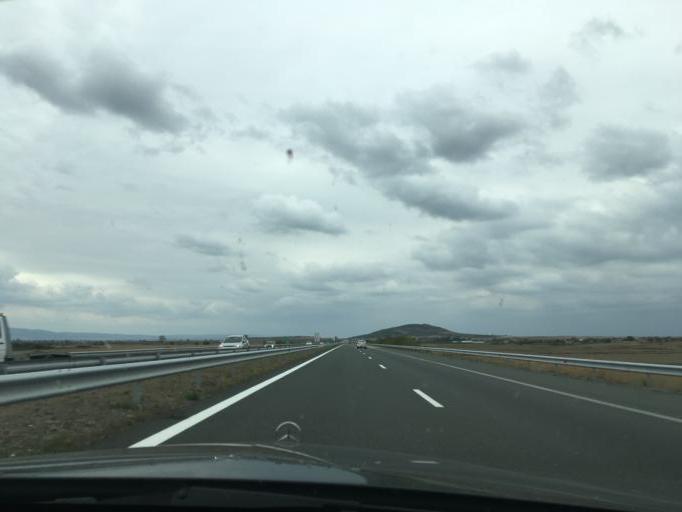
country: BG
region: Yambol
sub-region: Obshtina Yambol
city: Yambol
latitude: 42.5392
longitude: 26.4245
